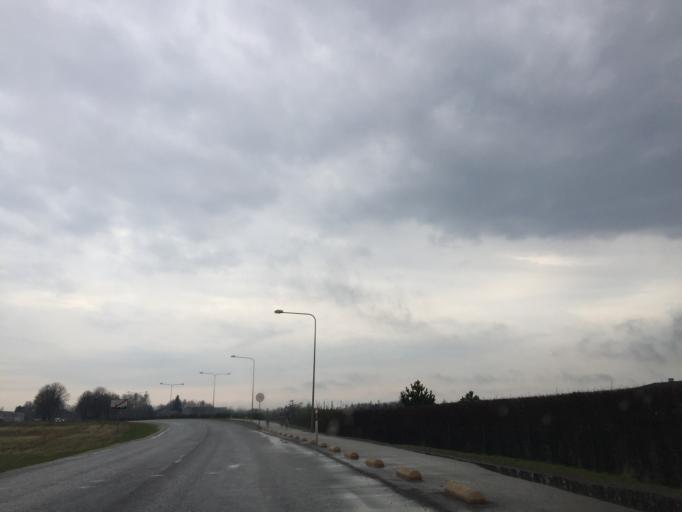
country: EE
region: Tartu
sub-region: UElenurme vald
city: Ulenurme
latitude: 58.3249
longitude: 26.7215
